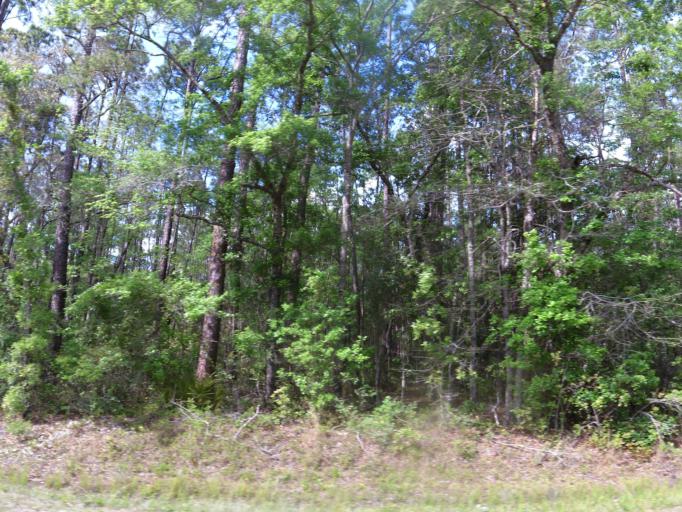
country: US
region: Georgia
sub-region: Charlton County
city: Folkston
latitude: 30.8064
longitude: -82.0414
